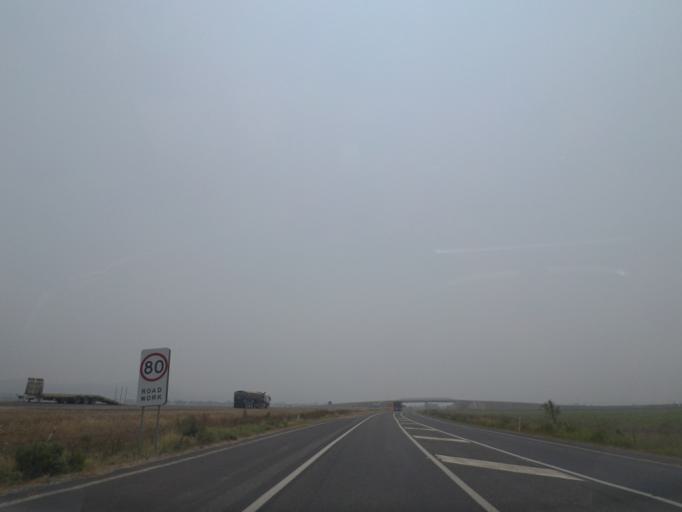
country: AU
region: New South Wales
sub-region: Clarence Valley
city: Maclean
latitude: -29.3970
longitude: 153.2394
